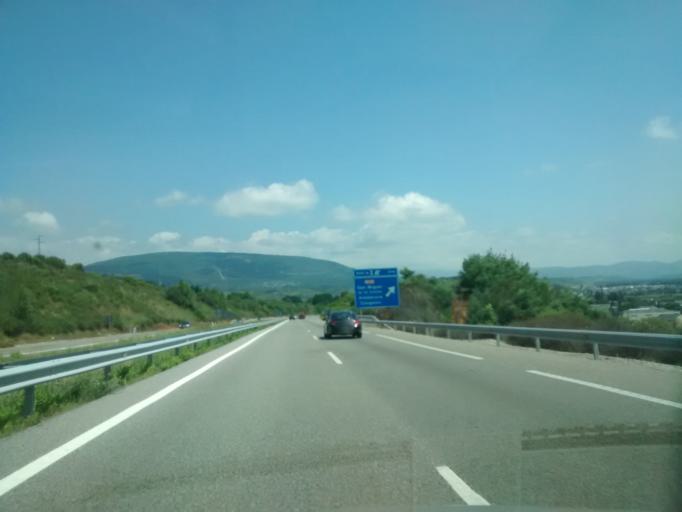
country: ES
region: Castille and Leon
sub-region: Provincia de Leon
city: Congosto
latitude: 42.5851
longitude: -6.5273
